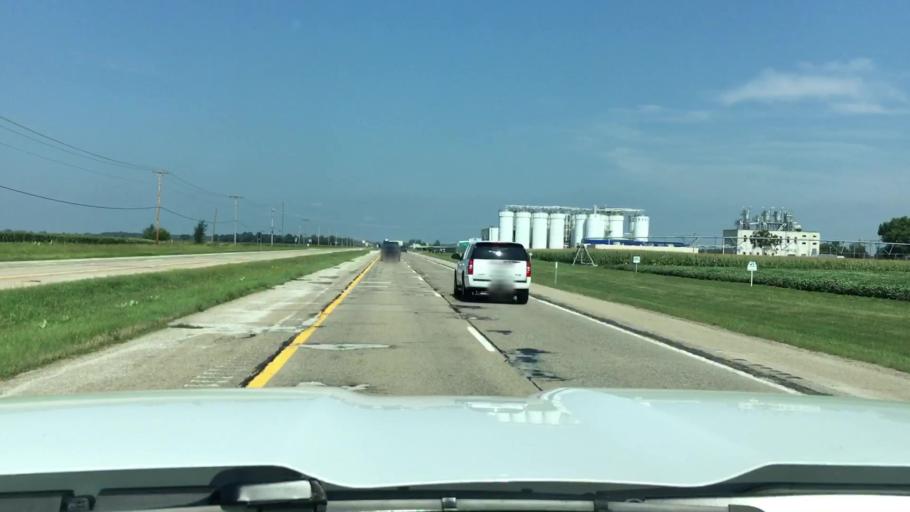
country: US
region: Michigan
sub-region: Kalamazoo County
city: Schoolcraft
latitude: 42.0752
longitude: -85.6365
